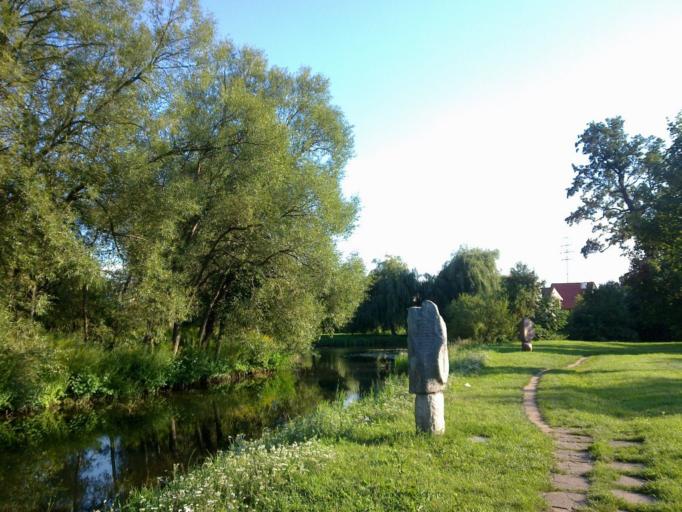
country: PL
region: Pomeranian Voivodeship
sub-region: Sopot
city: Sopot
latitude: 54.4160
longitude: 18.5739
